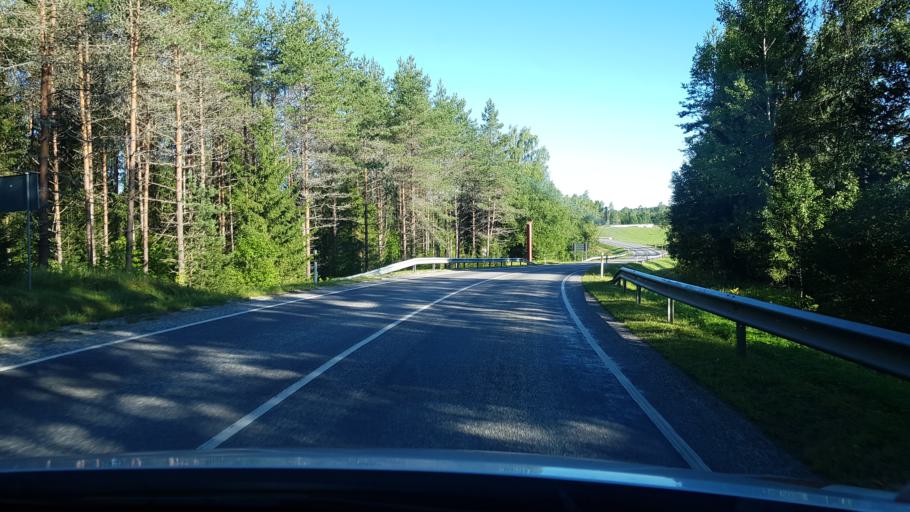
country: EE
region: Vorumaa
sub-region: Antsla vald
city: Vana-Antsla
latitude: 58.0185
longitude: 26.5869
